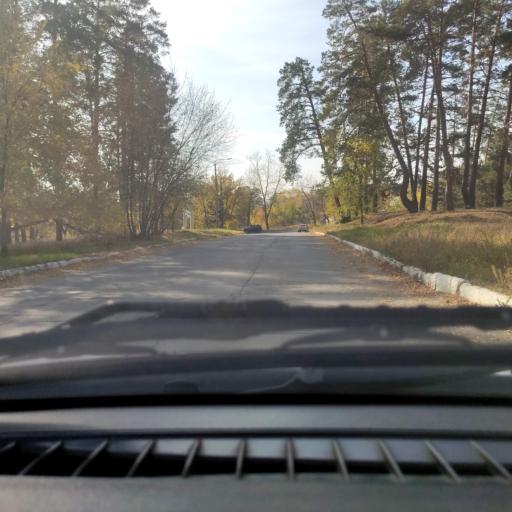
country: RU
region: Samara
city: Tol'yatti
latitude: 53.4749
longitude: 49.3794
